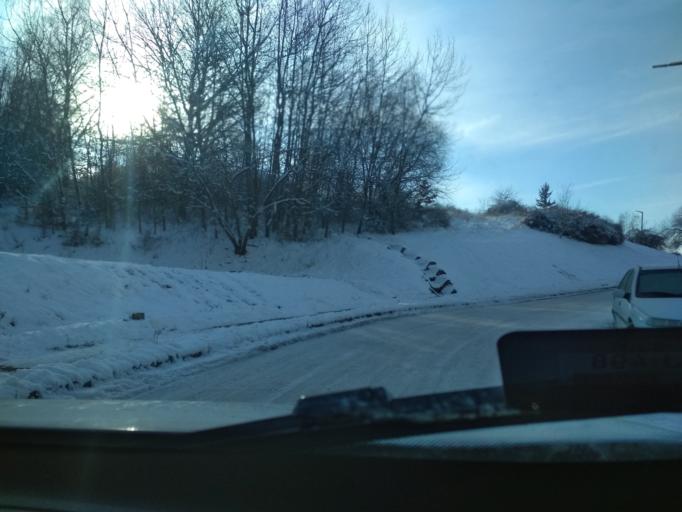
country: HU
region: Nograd
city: Salgotarjan
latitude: 48.1278
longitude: 19.8145
